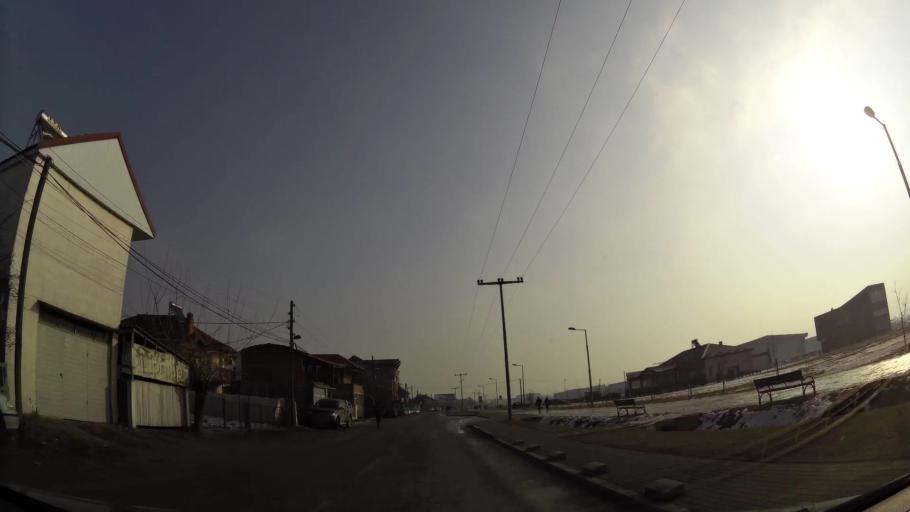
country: MK
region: Ilinden
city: Marino
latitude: 41.9870
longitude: 21.5887
